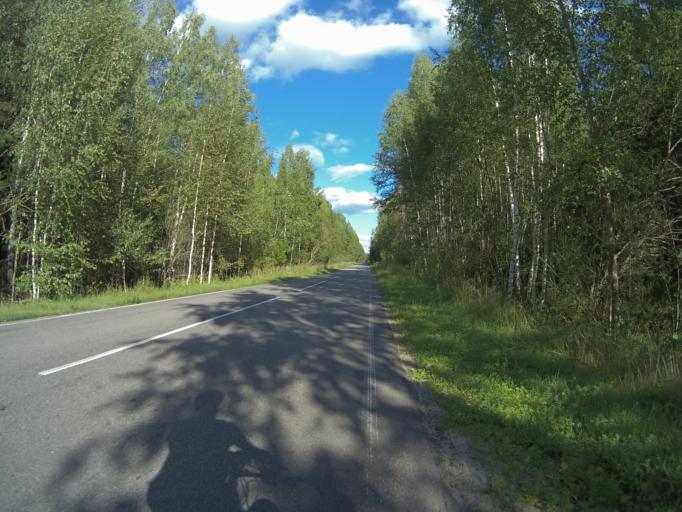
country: RU
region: Vladimir
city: Urshel'skiy
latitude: 55.6079
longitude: 40.2364
